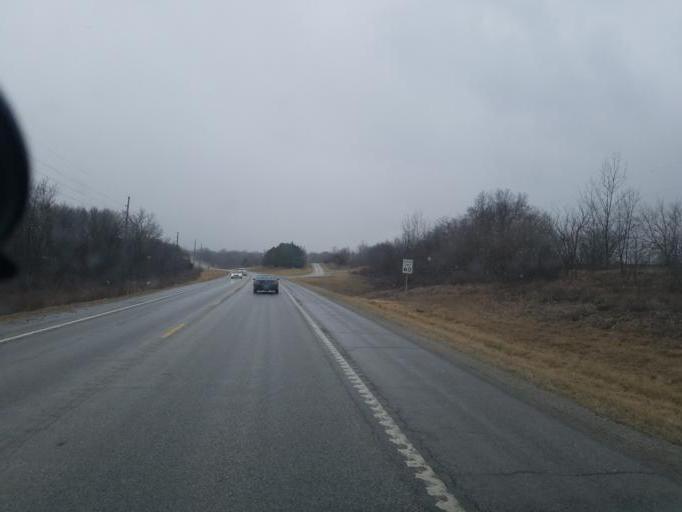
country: US
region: Missouri
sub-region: Schuyler County
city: Lancaster
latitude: 40.3649
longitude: -92.5626
